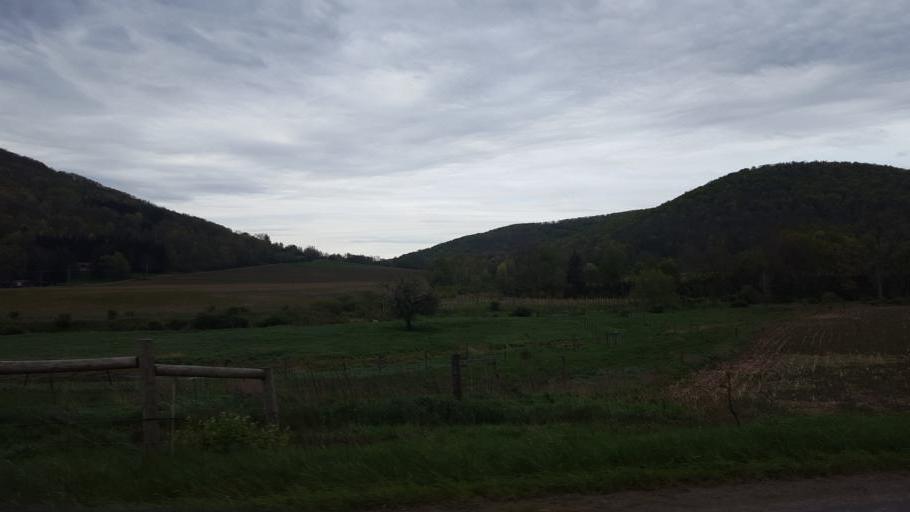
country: US
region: Pennsylvania
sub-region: Tioga County
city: Westfield
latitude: 41.9161
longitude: -77.5744
